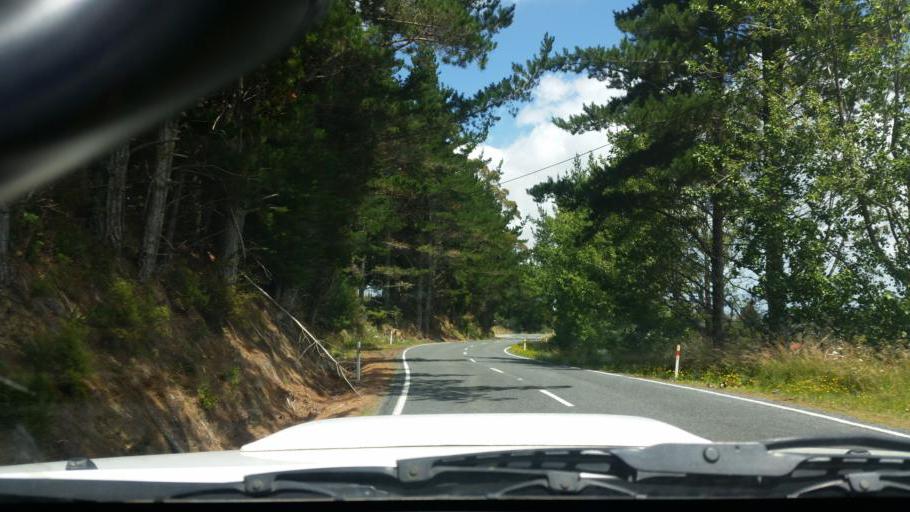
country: NZ
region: Northland
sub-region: Whangarei
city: Ruakaka
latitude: -36.0689
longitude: 174.2656
